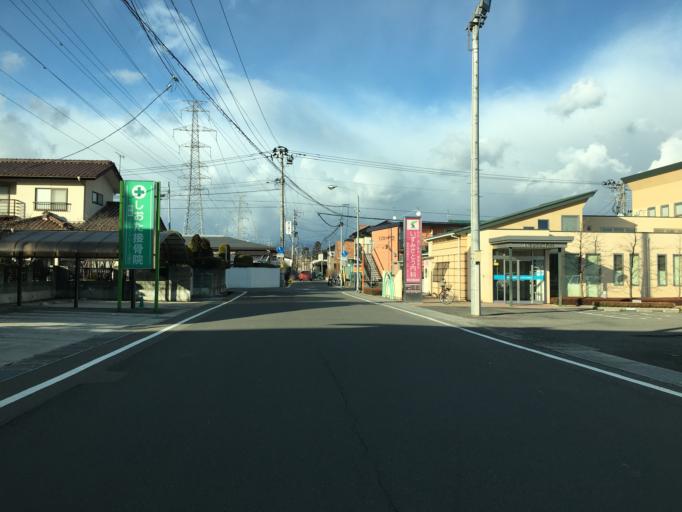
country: JP
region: Fukushima
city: Fukushima-shi
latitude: 37.7767
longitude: 140.4415
